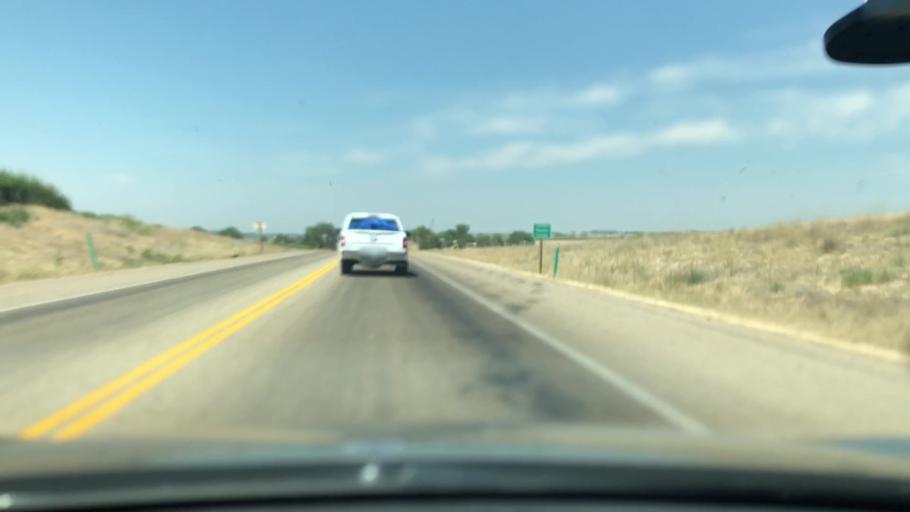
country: US
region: Idaho
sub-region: Canyon County
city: Parma
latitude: 43.8371
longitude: -116.9544
